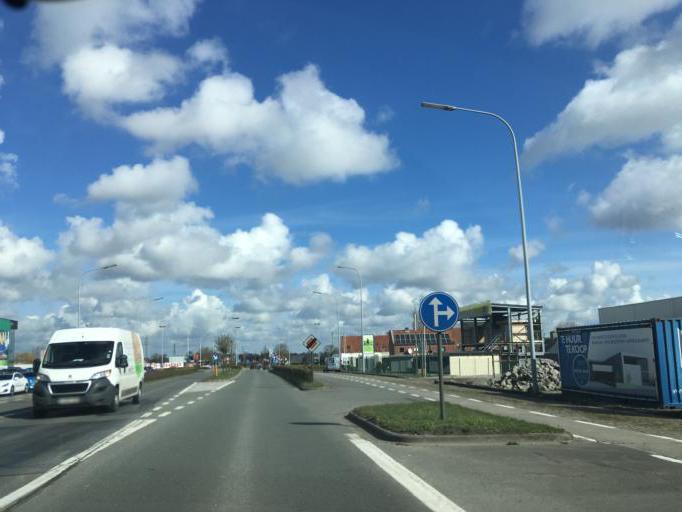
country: BE
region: Flanders
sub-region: Provincie West-Vlaanderen
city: Ledegem
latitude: 50.8995
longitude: 3.1149
